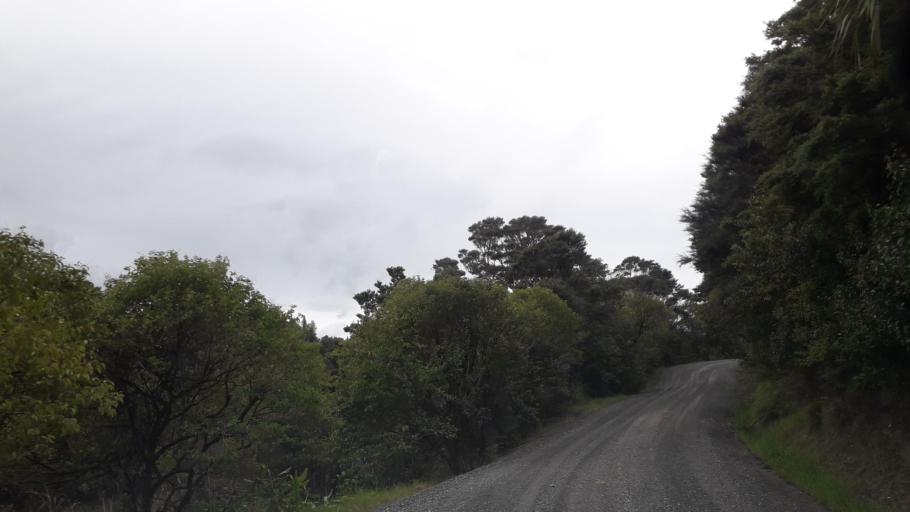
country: NZ
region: Northland
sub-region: Far North District
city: Waimate North
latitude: -35.3051
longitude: 173.5629
